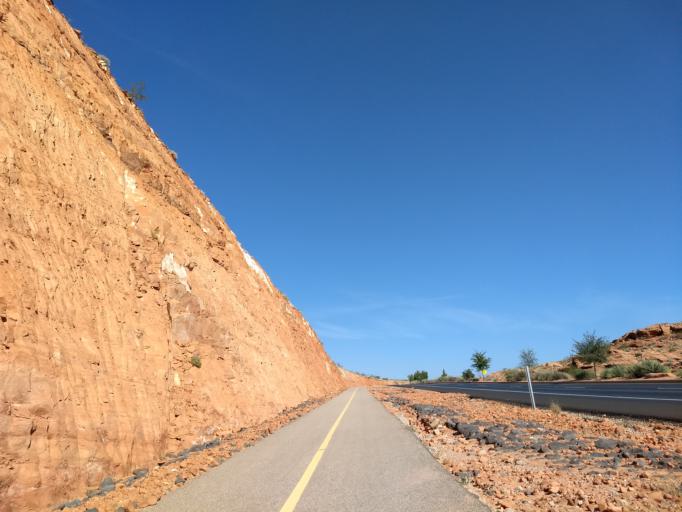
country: US
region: Utah
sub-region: Washington County
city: Saint George
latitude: 37.1212
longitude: -113.5839
